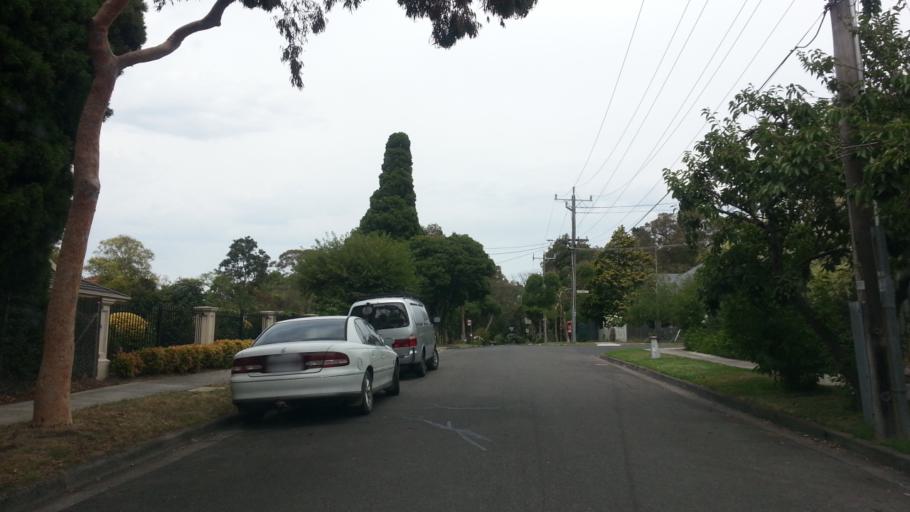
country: AU
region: Victoria
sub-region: Whitehorse
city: Vermont
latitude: -37.8281
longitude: 145.2007
